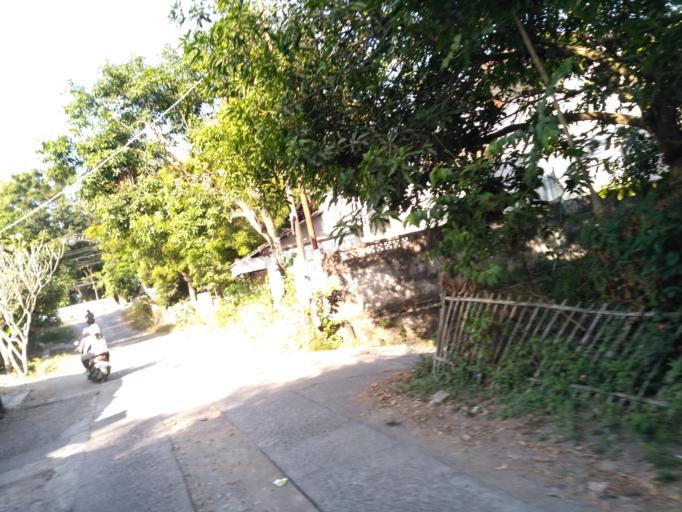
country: ID
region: Daerah Istimewa Yogyakarta
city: Depok
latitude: -7.7729
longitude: 110.4301
